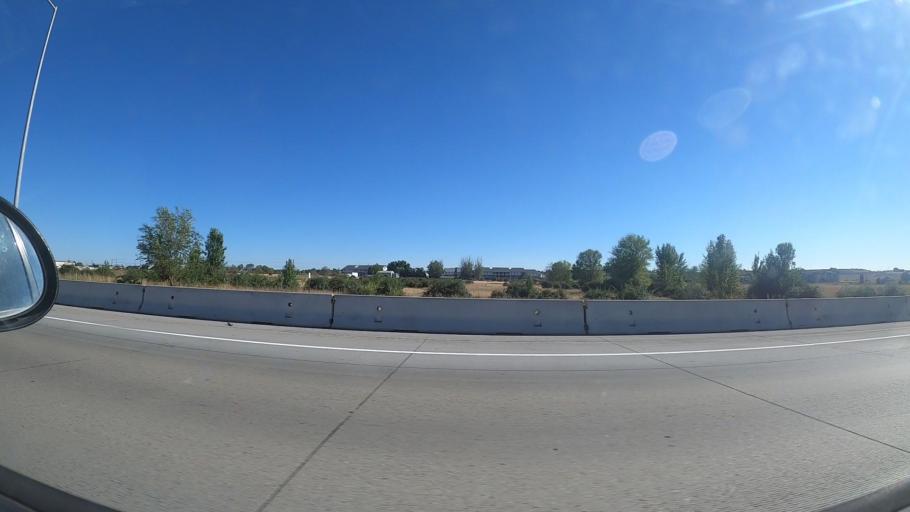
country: US
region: Idaho
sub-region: Ada County
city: Meridian
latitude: 43.5933
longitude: -116.4246
